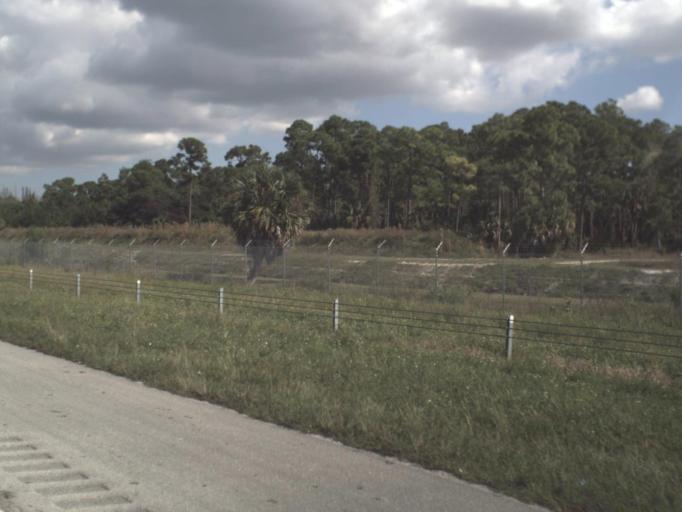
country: US
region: Florida
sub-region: Palm Beach County
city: Lake Belvedere Estates
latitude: 26.6656
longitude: -80.1738
